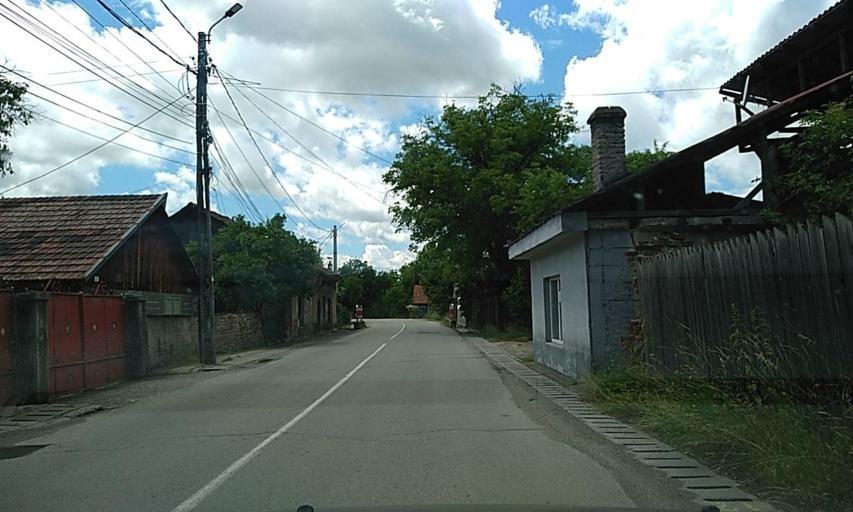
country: RO
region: Hunedoara
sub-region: Oras Petrila
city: Petrila
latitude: 45.4552
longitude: 23.4378
